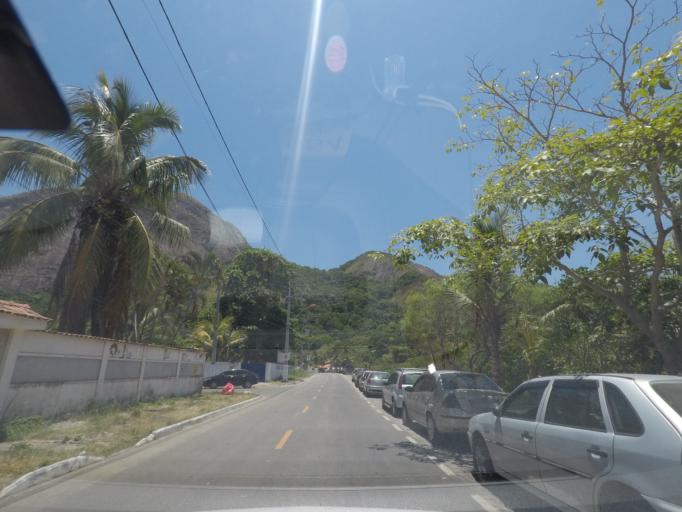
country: BR
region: Rio de Janeiro
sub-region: Niteroi
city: Niteroi
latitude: -22.9694
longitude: -43.0124
